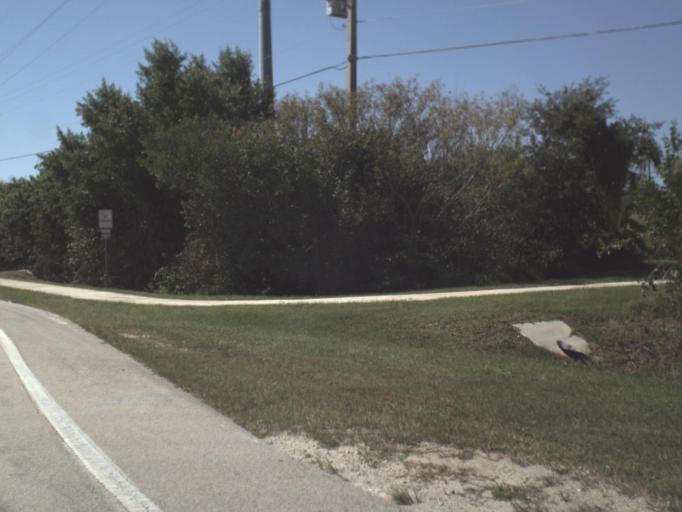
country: US
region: Florida
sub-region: Collier County
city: Marco
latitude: 25.9838
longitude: -81.7026
